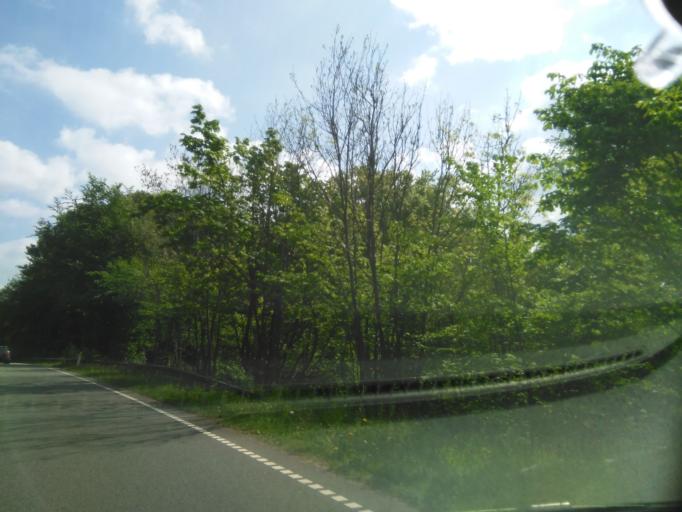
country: DK
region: Central Jutland
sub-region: Skanderborg Kommune
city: Skanderborg
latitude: 56.0292
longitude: 9.9591
